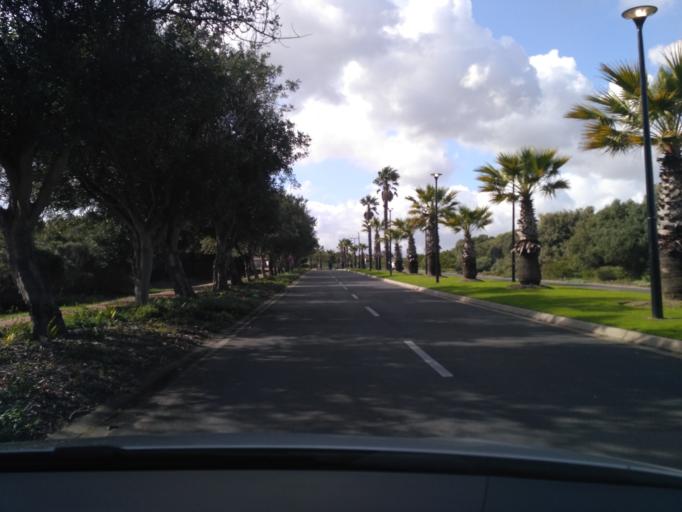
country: ZA
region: Western Cape
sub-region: City of Cape Town
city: Kraaifontein
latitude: -33.9349
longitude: 18.6208
